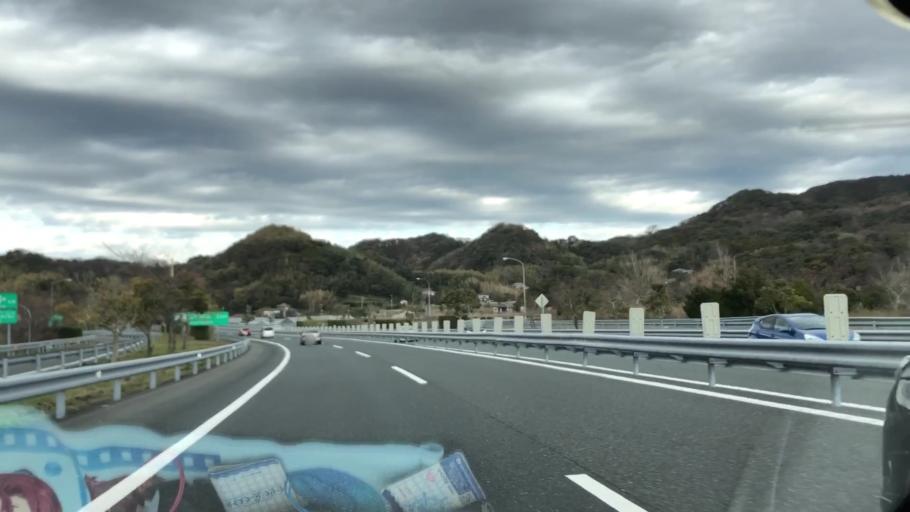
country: JP
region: Chiba
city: Tateyama
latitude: 35.0983
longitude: 139.8591
